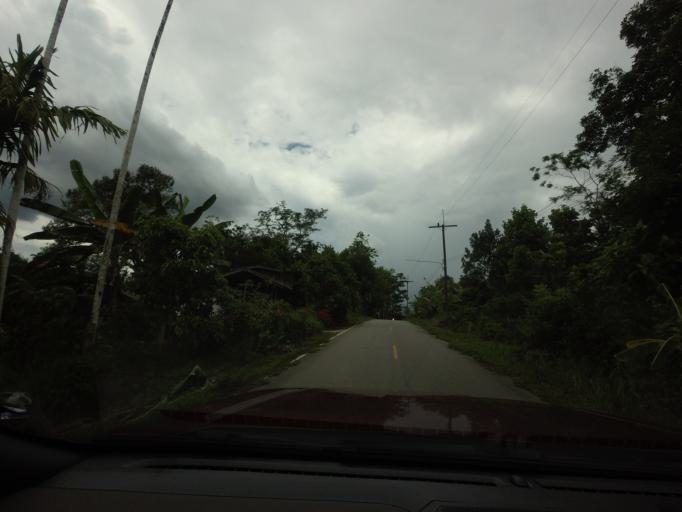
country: TH
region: Narathiwat
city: Sukhirin
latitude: 5.9877
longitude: 101.7063
